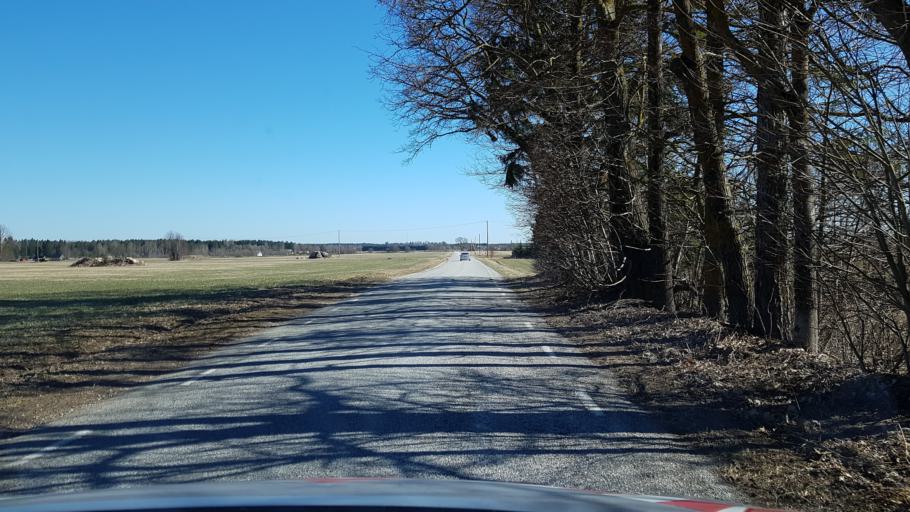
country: EE
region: Laeaene-Virumaa
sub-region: Viru-Nigula vald
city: Kunda
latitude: 59.4076
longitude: 26.5340
